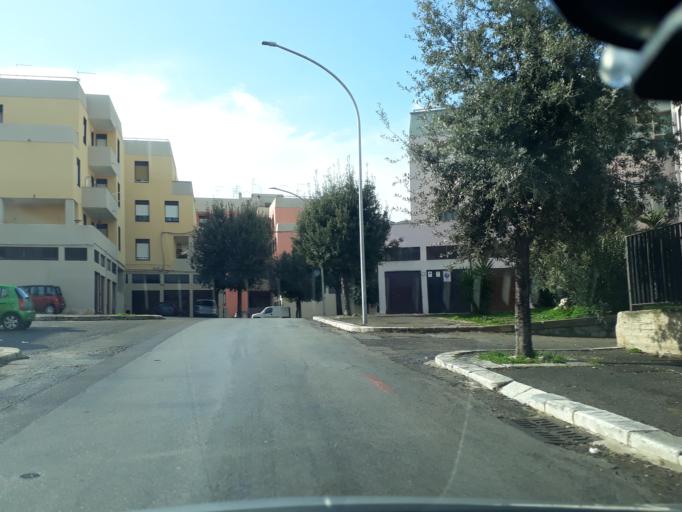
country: IT
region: Apulia
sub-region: Provincia di Brindisi
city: Fasano
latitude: 40.8283
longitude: 17.3574
